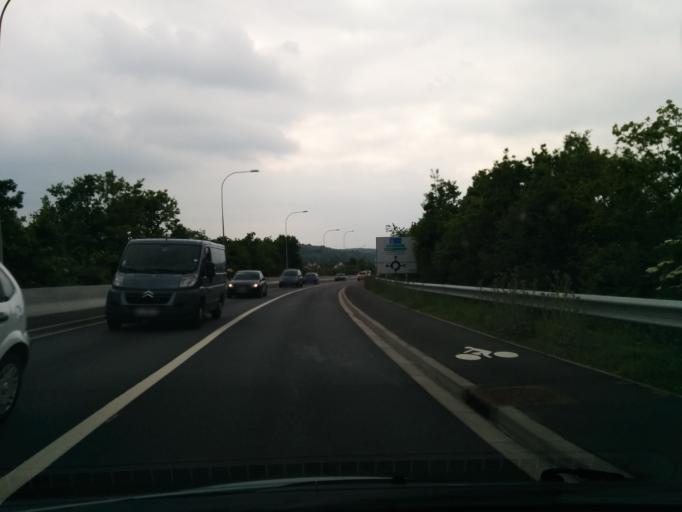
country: FR
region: Ile-de-France
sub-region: Departement des Yvelines
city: Flins-sur-Seine
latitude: 48.9700
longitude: 1.8752
